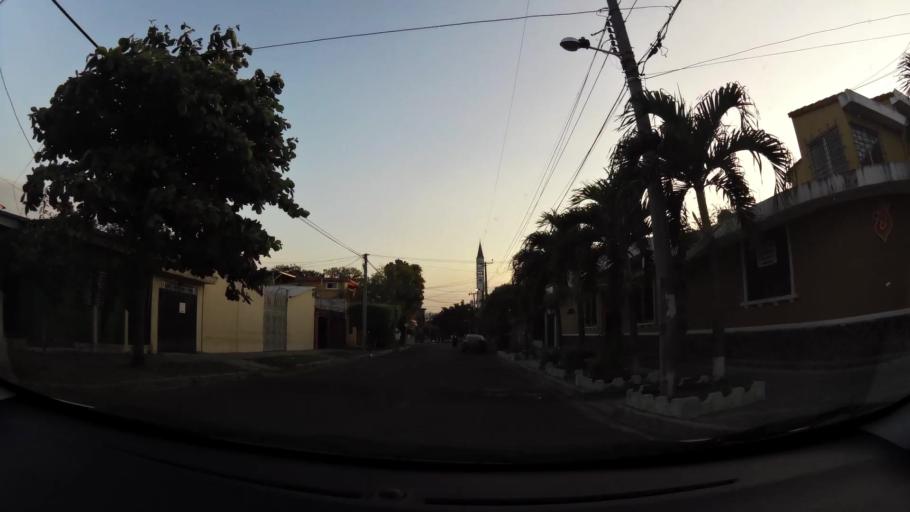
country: SV
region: San Salvador
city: Delgado
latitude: 13.7149
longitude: -89.1917
